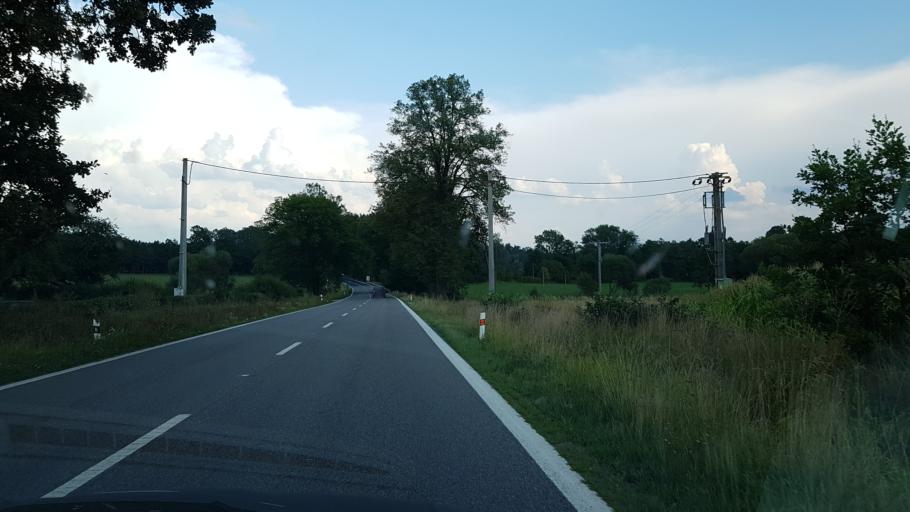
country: CZ
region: Pardubicky
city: Zamberk
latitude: 50.0984
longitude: 16.4069
